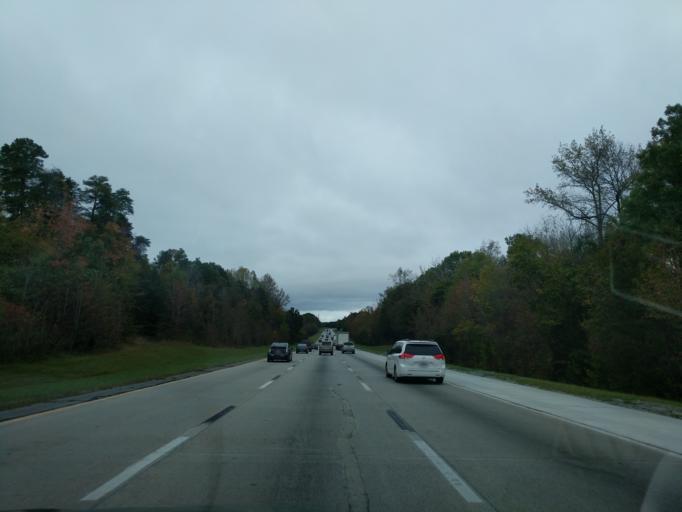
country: US
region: North Carolina
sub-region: Guilford County
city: Jamestown
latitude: 35.9686
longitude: -79.8919
